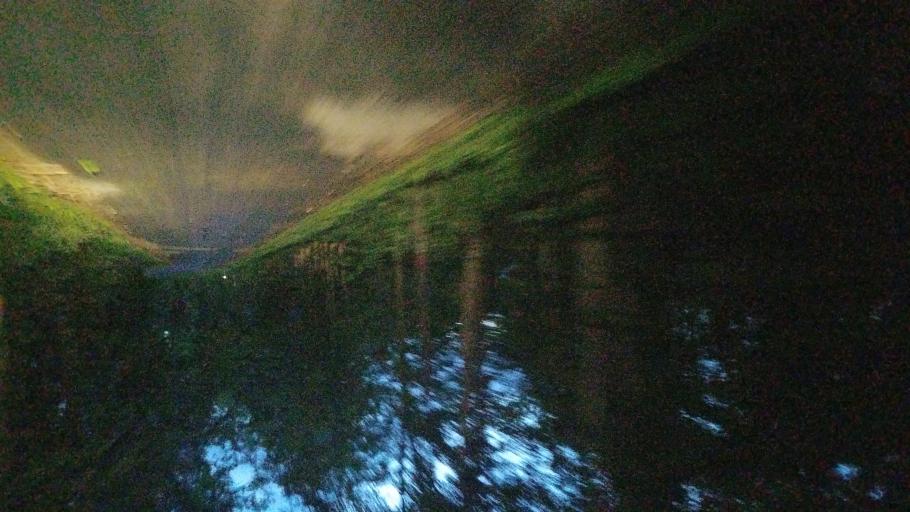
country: US
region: New York
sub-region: Wayne County
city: Clyde
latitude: 43.0447
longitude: -76.9071
